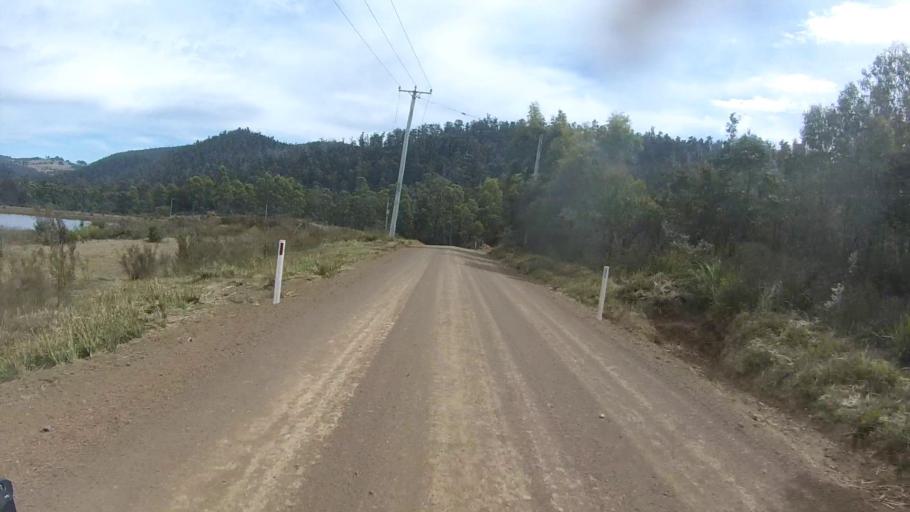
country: AU
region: Tasmania
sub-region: Sorell
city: Sorell
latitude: -42.7554
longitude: 147.7999
